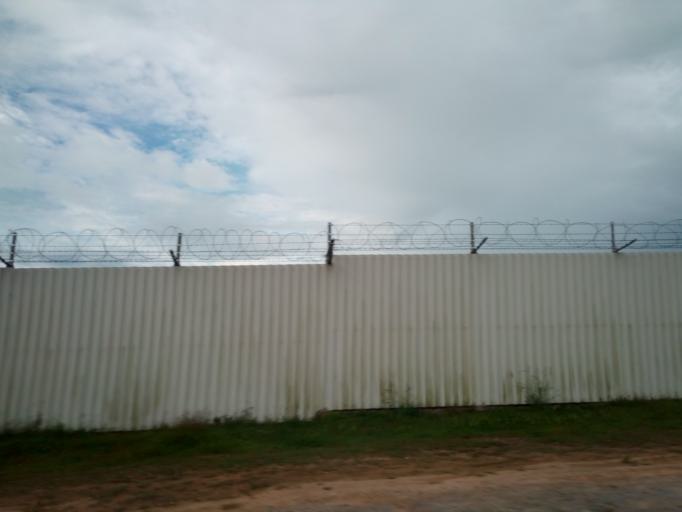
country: TH
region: Phuket
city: Thalang
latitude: 8.1127
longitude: 98.3301
